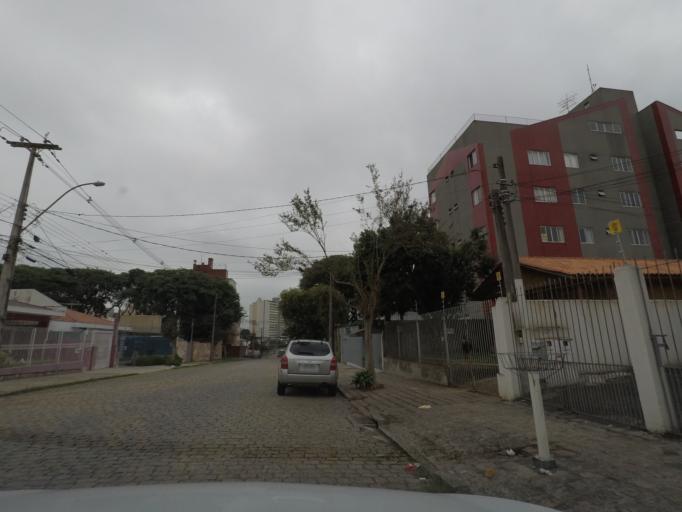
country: BR
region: Parana
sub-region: Curitiba
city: Curitiba
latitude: -25.4385
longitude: -49.2487
